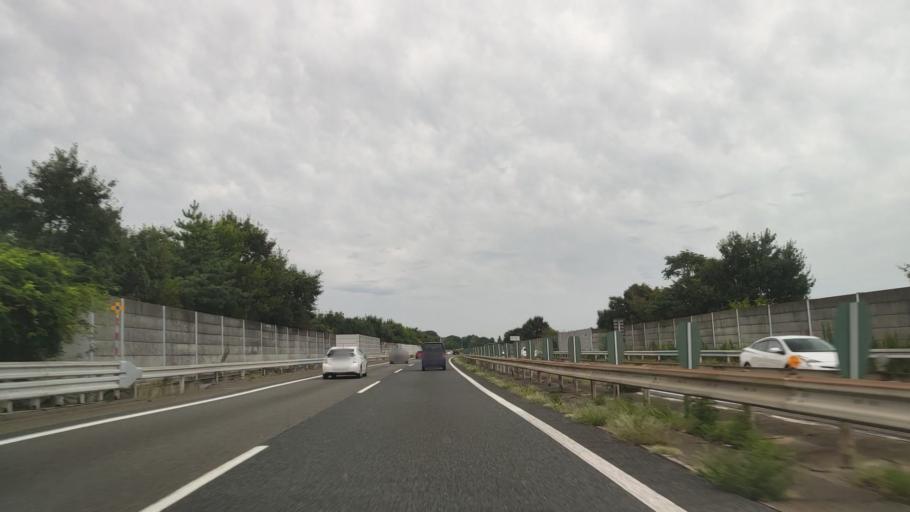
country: JP
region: Shiga Prefecture
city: Hikone
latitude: 35.2304
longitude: 136.2830
